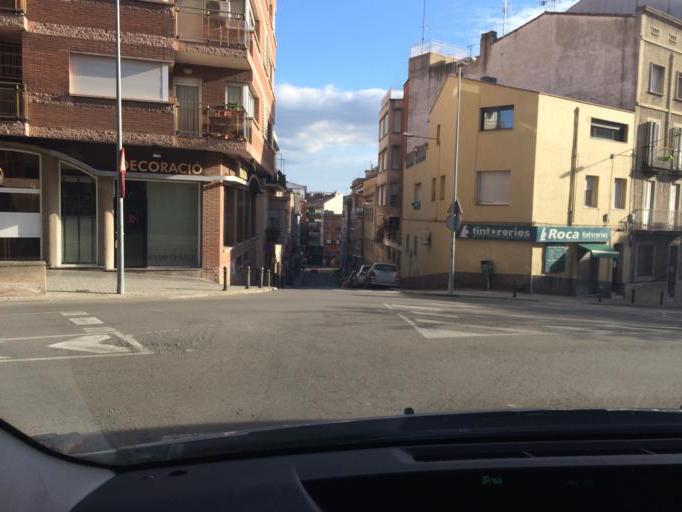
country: ES
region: Catalonia
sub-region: Provincia de Barcelona
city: Manresa
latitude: 41.7269
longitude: 1.8205
